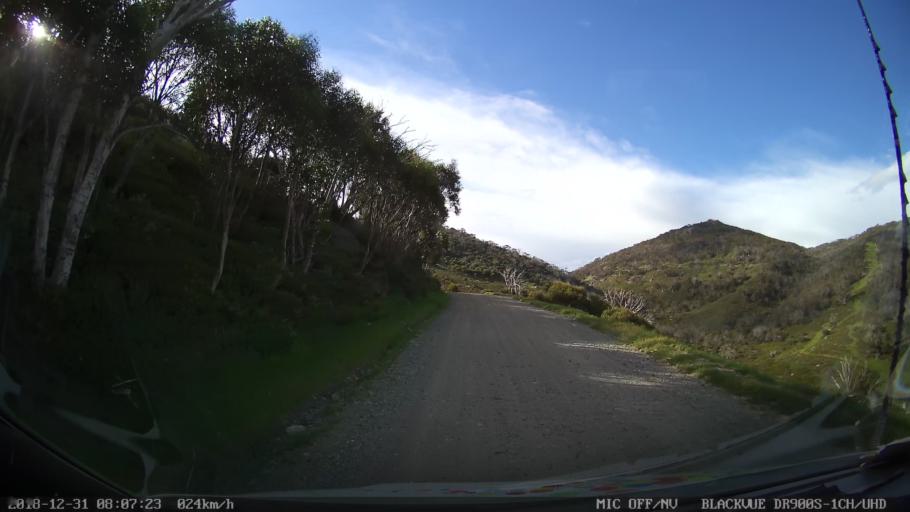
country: AU
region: New South Wales
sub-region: Snowy River
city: Jindabyne
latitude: -36.3787
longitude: 148.4091
